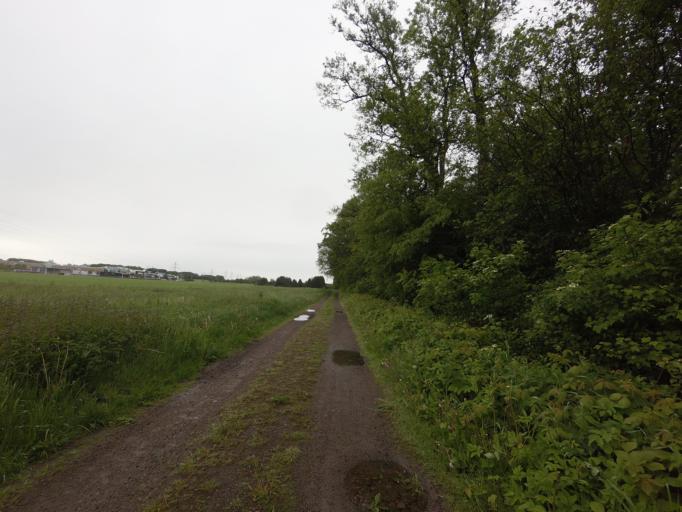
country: SE
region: Skane
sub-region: Helsingborg
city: Odakra
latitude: 56.0900
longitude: 12.7362
